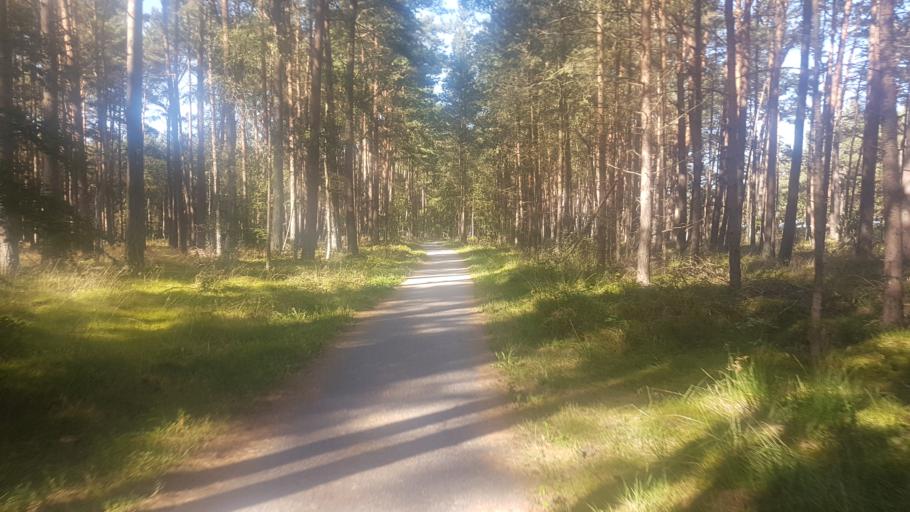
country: DE
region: Mecklenburg-Vorpommern
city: Glowe
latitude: 54.5787
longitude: 13.4114
